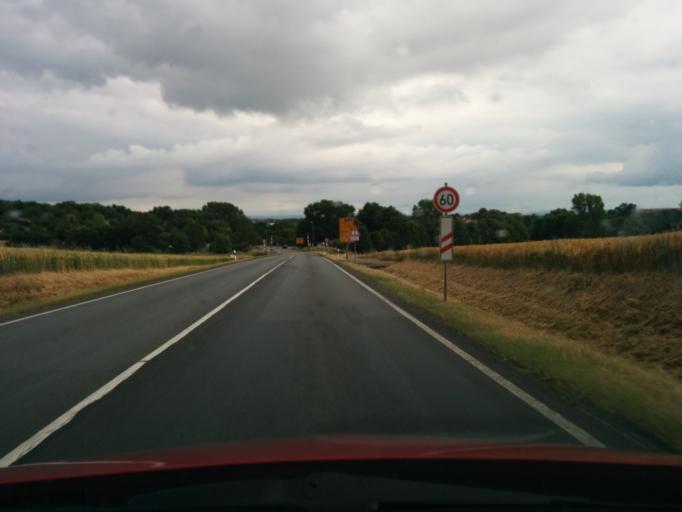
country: DE
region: Thuringia
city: Straussfurt
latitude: 51.1729
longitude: 10.9883
